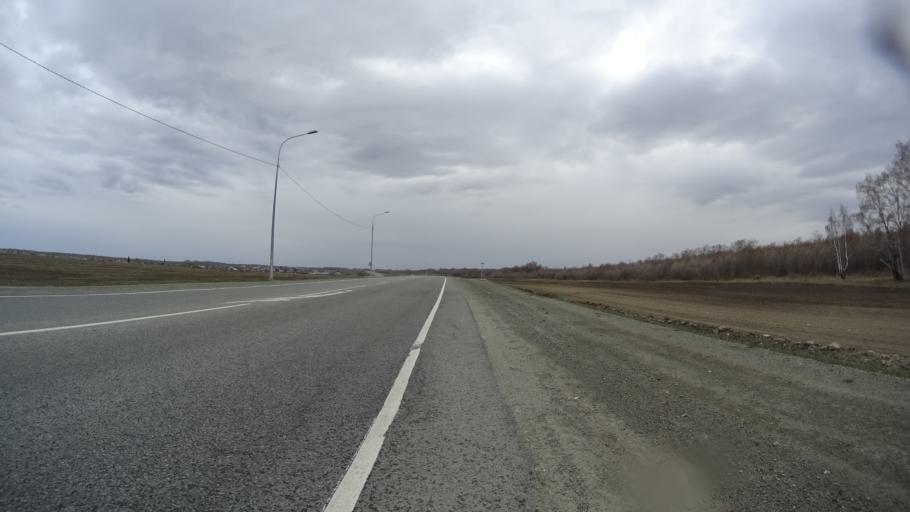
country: RU
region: Chelyabinsk
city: Krasnogorskiy
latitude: 54.6813
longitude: 61.2469
